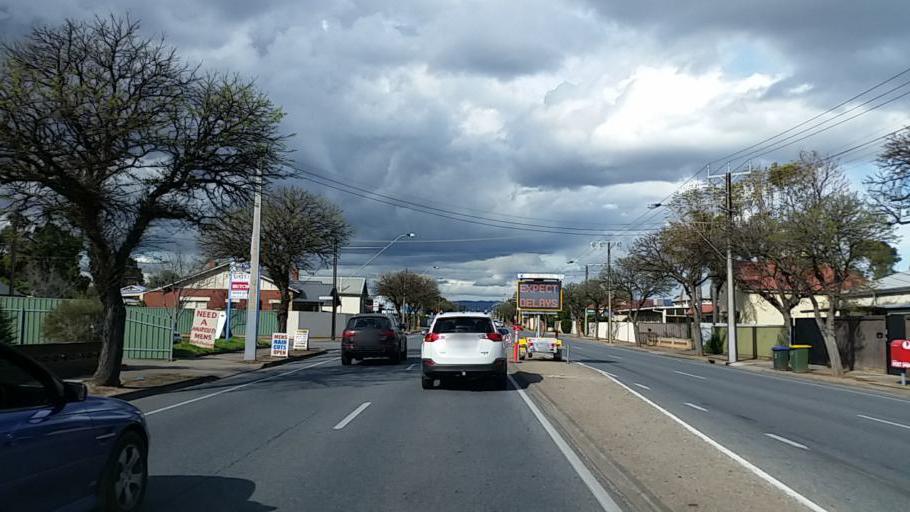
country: AU
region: South Australia
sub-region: Charles Sturt
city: Allenby Gardens
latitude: -34.9041
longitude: 138.5612
